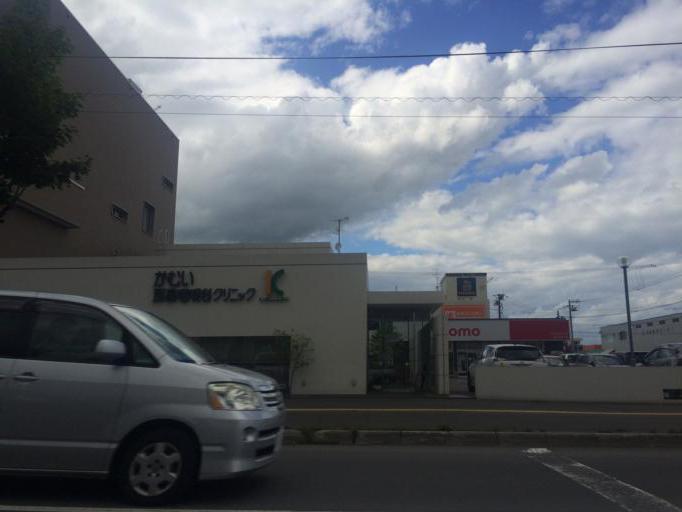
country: JP
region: Hokkaido
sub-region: Asahikawa-shi
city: Asahikawa
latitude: 43.7593
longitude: 142.3370
